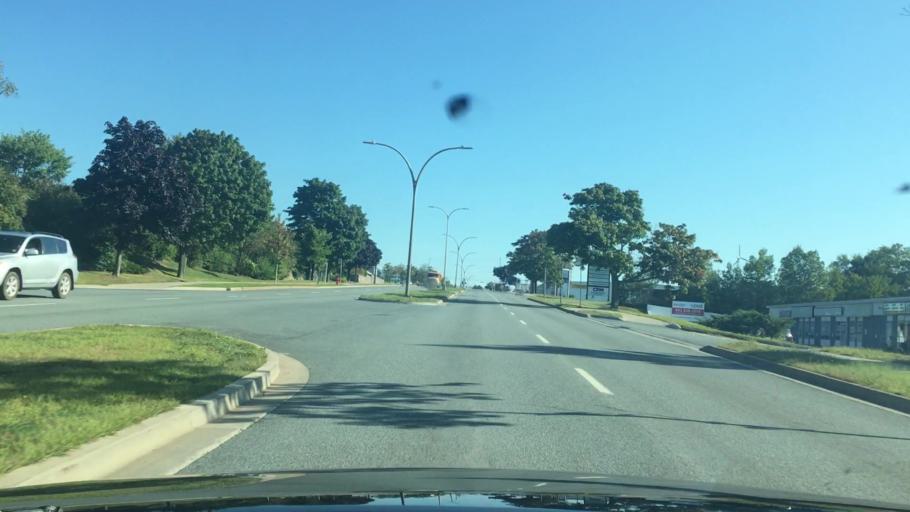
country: CA
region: Nova Scotia
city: Dartmouth
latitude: 44.7050
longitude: -63.6103
